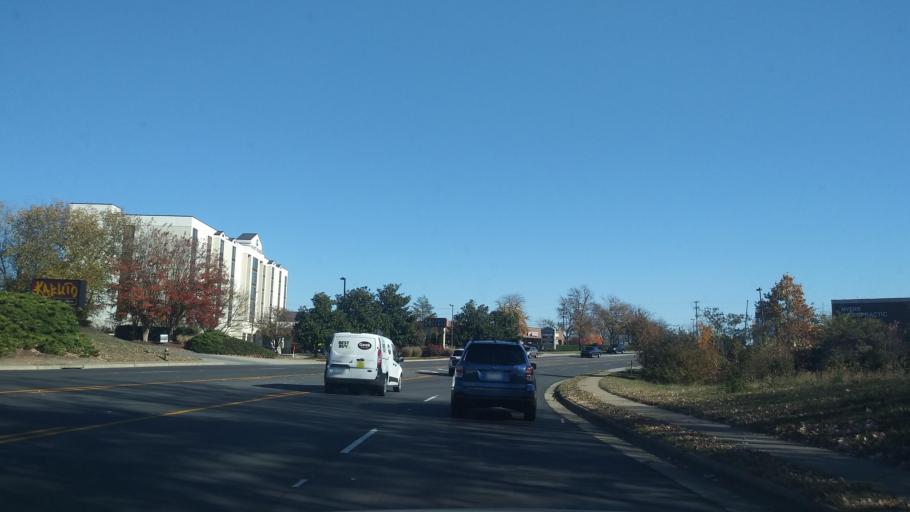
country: US
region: North Carolina
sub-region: Guilford County
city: Jamestown
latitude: 36.0543
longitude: -79.8926
